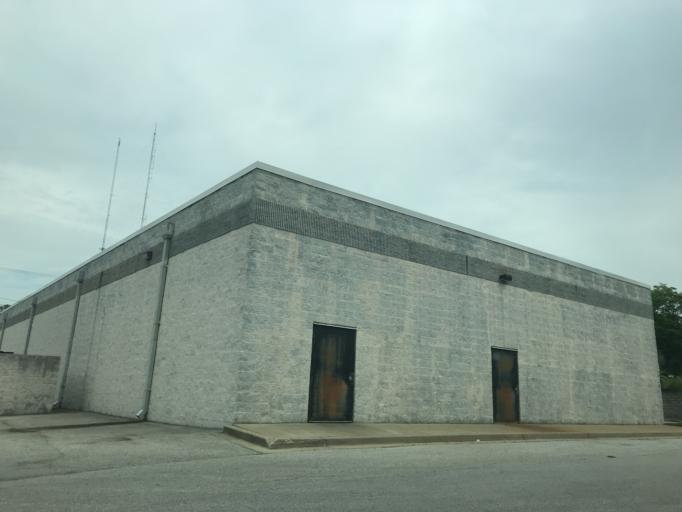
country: US
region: Maryland
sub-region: Baltimore County
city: Catonsville
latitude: 39.2836
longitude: -76.7579
